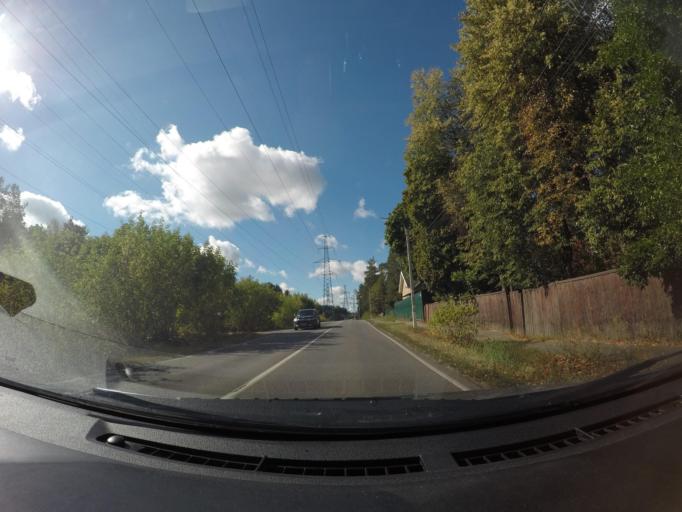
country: RU
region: Moskovskaya
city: Zhukovskiy
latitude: 55.6084
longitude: 38.1358
